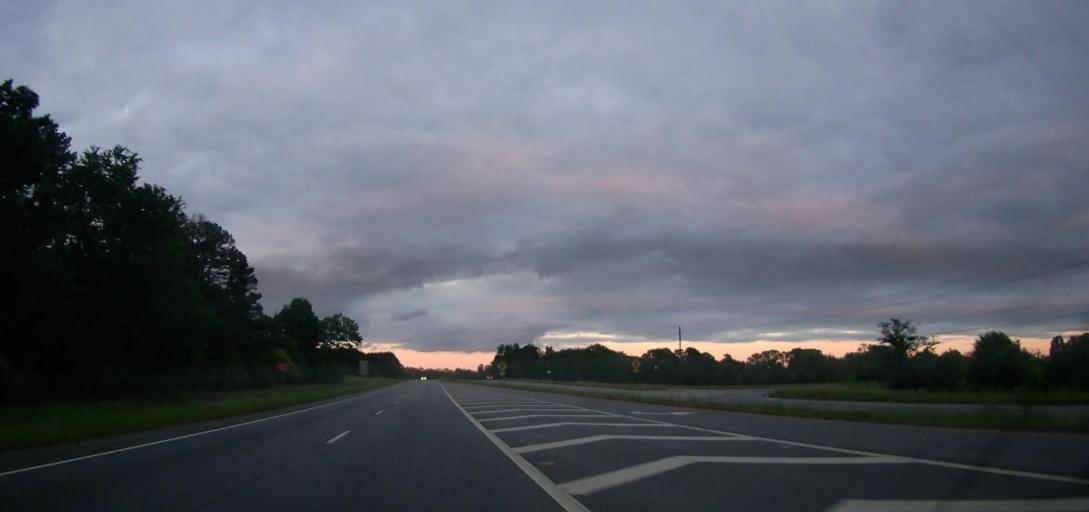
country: US
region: Georgia
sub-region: Jackson County
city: Arcade
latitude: 34.0618
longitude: -83.5189
